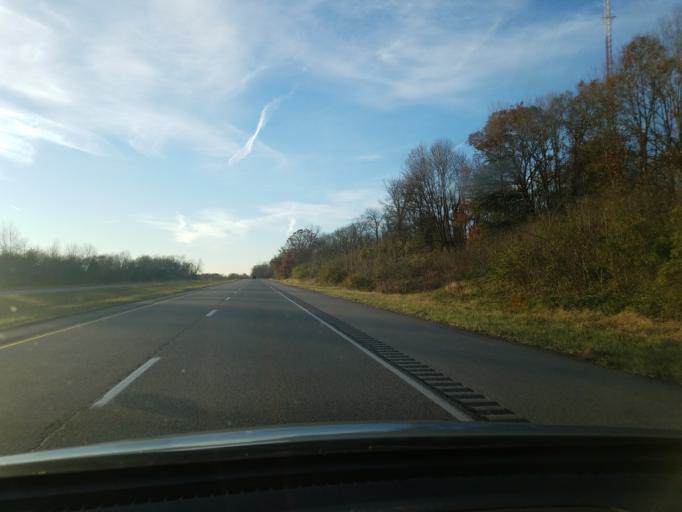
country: US
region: Indiana
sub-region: Warrick County
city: Boonville
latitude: 38.2017
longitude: -87.2011
